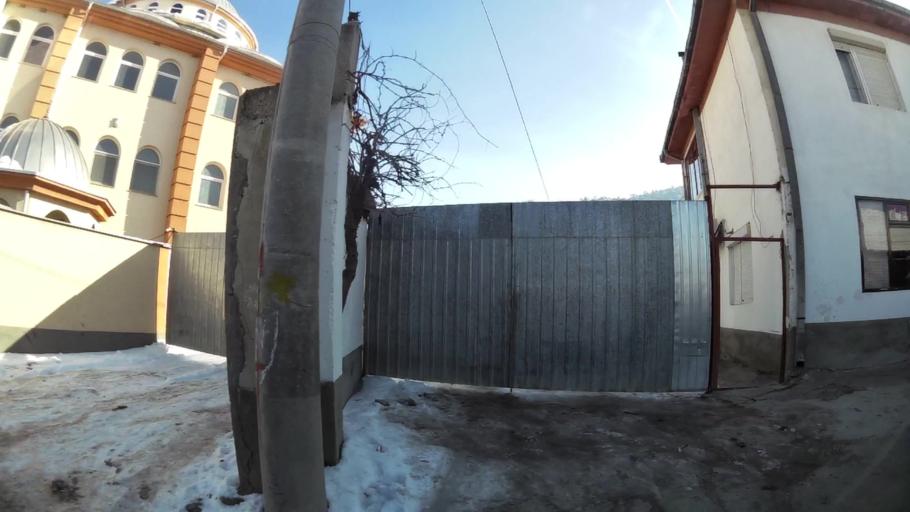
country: MK
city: Grchec
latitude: 41.9949
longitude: 21.3419
